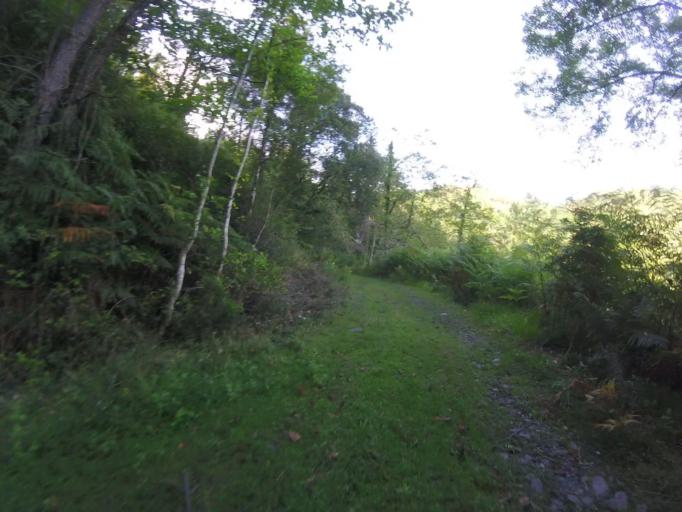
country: ES
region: Navarre
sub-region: Provincia de Navarra
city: Arano
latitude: 43.2273
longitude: -1.9130
